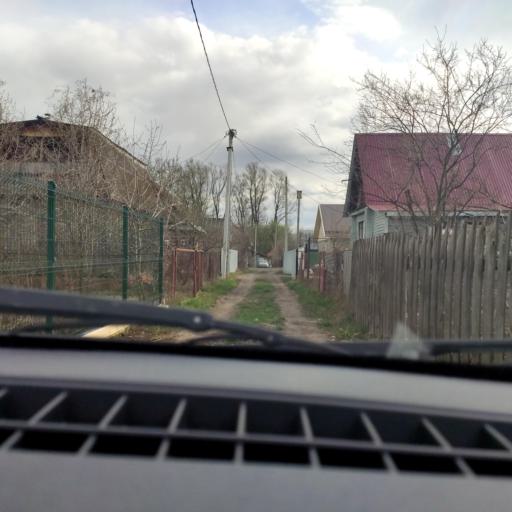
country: RU
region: Bashkortostan
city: Mikhaylovka
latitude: 54.7945
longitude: 55.8365
